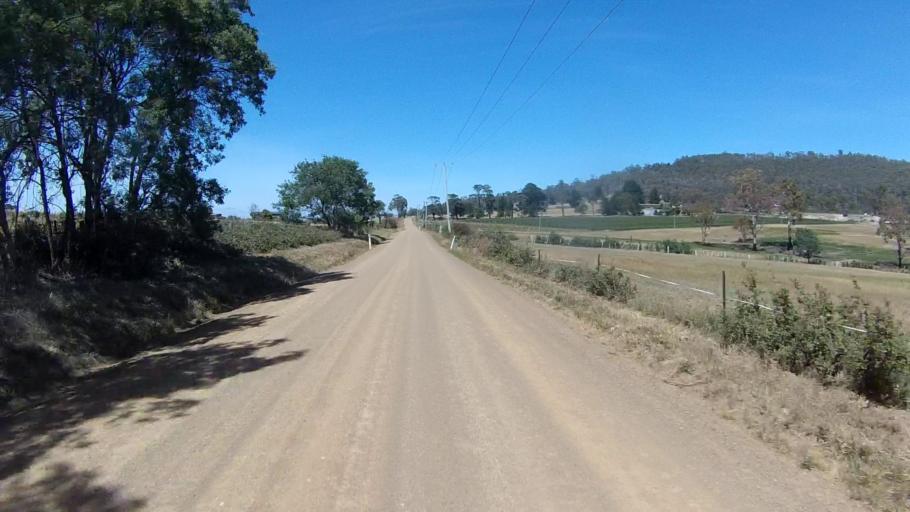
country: AU
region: Tasmania
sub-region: Sorell
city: Sorell
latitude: -42.7841
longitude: 147.6390
